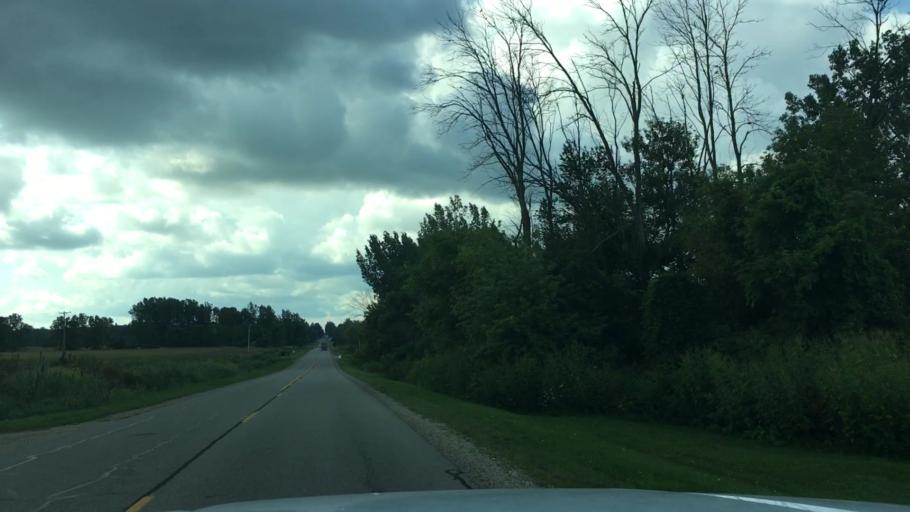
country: US
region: Michigan
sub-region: Ottawa County
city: Hudsonville
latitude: 42.7925
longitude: -85.8418
